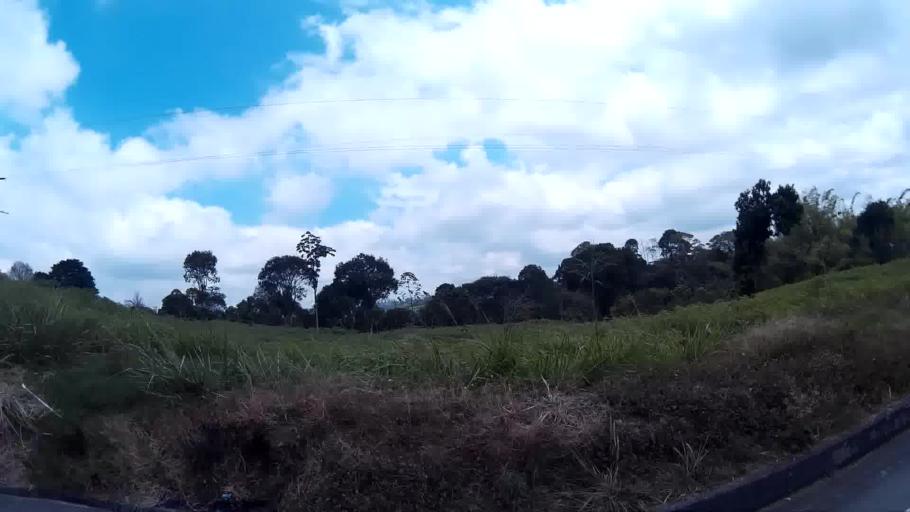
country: CO
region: Quindio
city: Circasia
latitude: 4.5882
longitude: -75.6428
